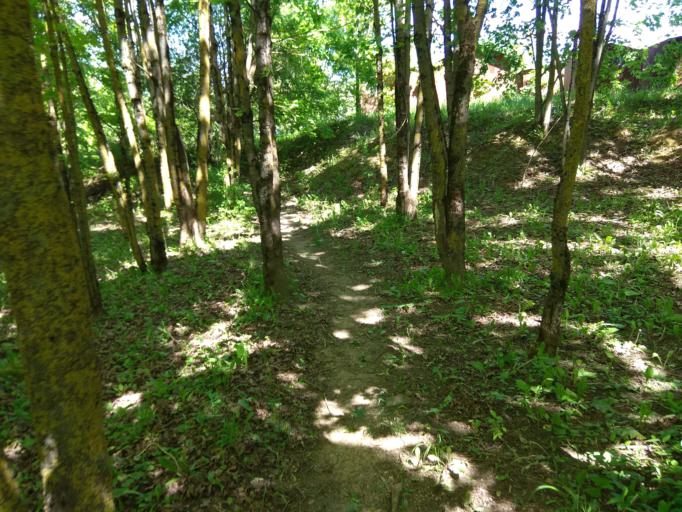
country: BY
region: Grodnenskaya
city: Hrodna
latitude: 53.7133
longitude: 23.7989
